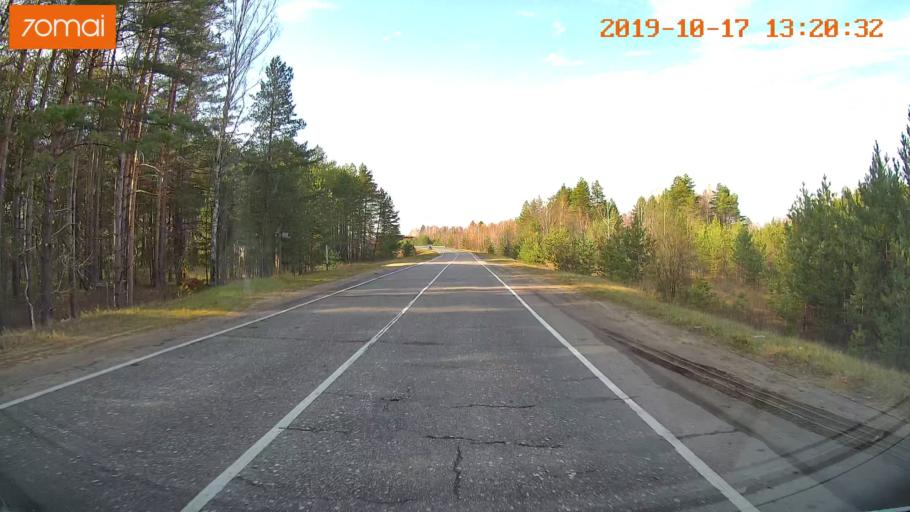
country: RU
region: Rjazan
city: Gus'-Zheleznyy
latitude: 55.0767
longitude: 41.0483
